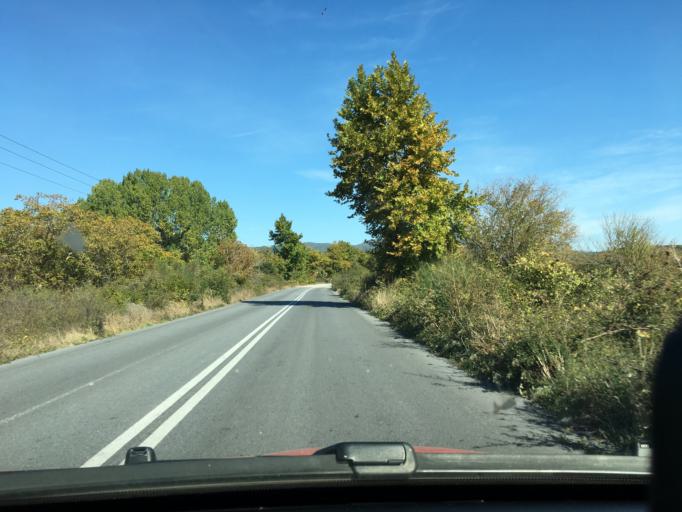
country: GR
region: Central Macedonia
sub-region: Nomos Chalkidikis
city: Megali Panagia
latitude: 40.3763
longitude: 23.6959
